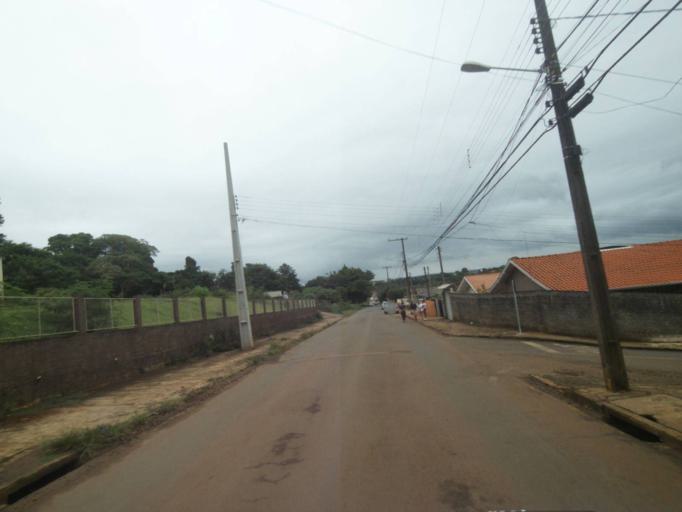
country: BR
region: Parana
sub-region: Telemaco Borba
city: Telemaco Borba
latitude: -24.3295
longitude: -50.6478
